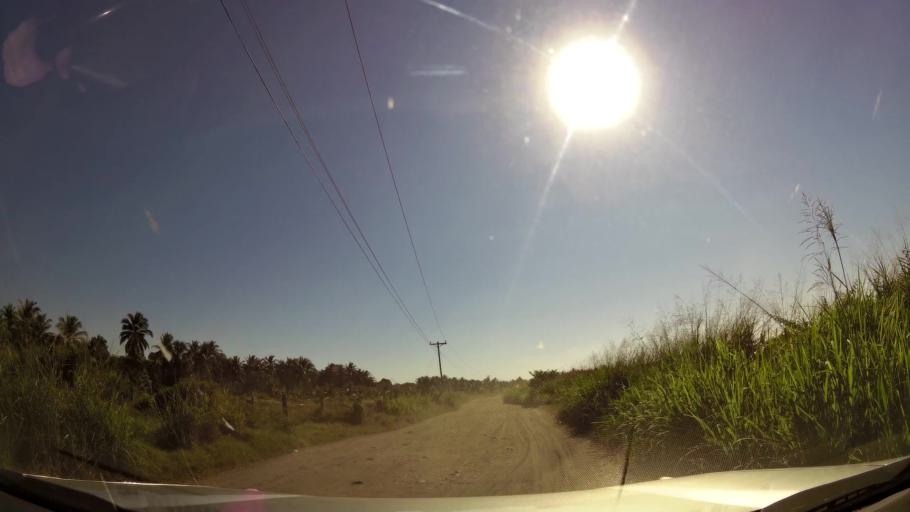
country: GT
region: Santa Rosa
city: Guazacapan
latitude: 13.8586
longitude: -90.3925
